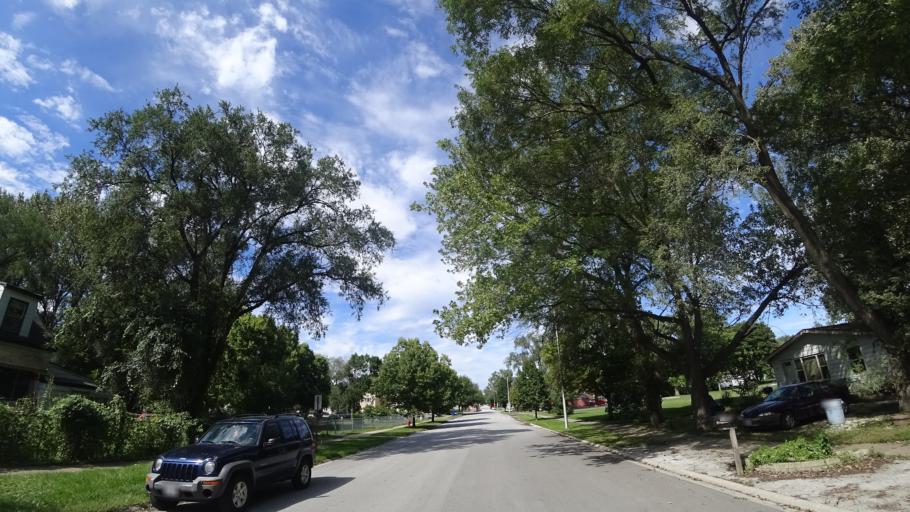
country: US
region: Illinois
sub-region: Cook County
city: Chicago Ridge
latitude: 41.7111
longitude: -87.7746
